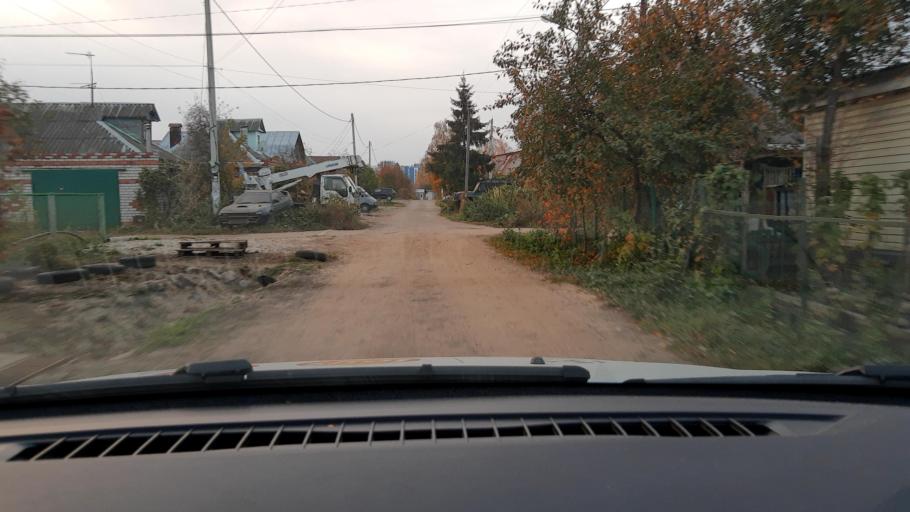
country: RU
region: Nizjnij Novgorod
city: Burevestnik
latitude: 56.2125
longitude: 43.8144
